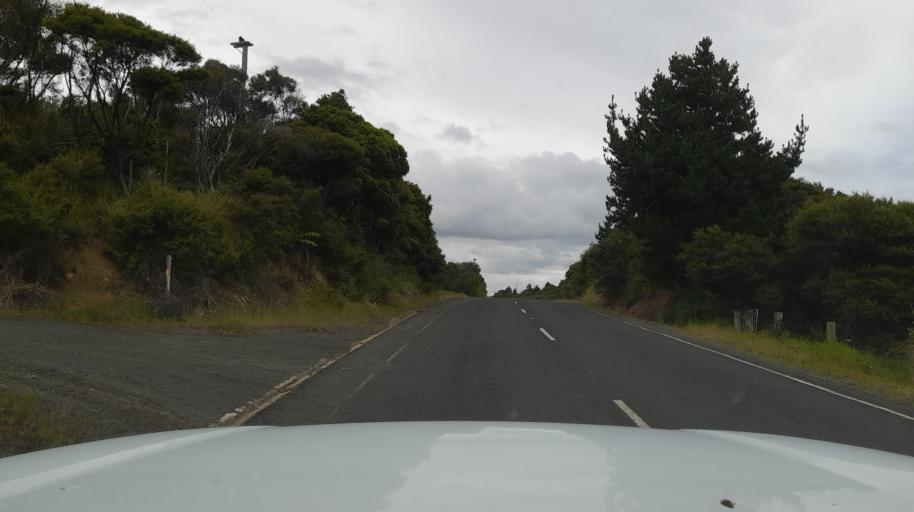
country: NZ
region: Northland
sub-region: Far North District
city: Kaitaia
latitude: -35.3627
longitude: 173.4048
